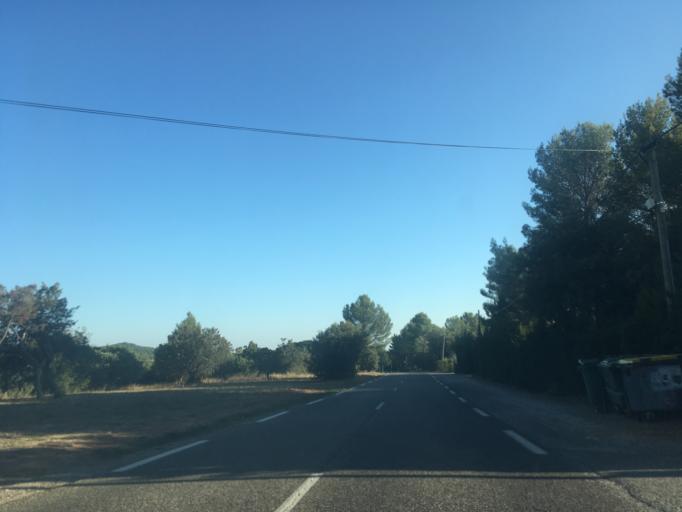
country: FR
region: Provence-Alpes-Cote d'Azur
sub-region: Departement du Var
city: Aups
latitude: 43.6161
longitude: 6.2255
